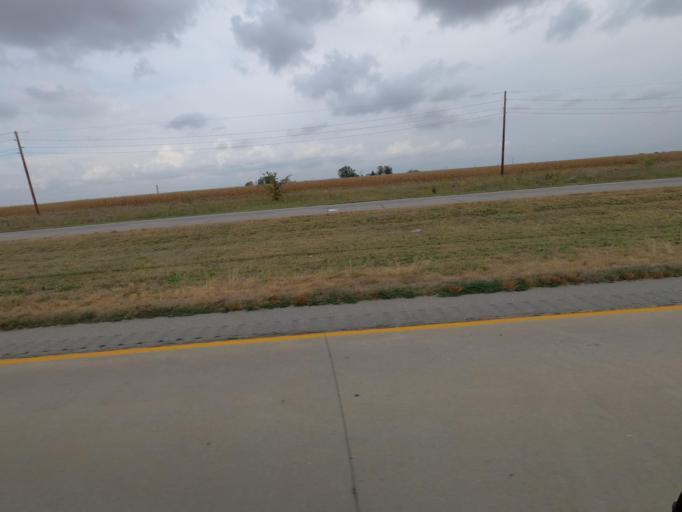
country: US
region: Iowa
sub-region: Jasper County
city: Monroe
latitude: 41.5684
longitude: -93.1631
